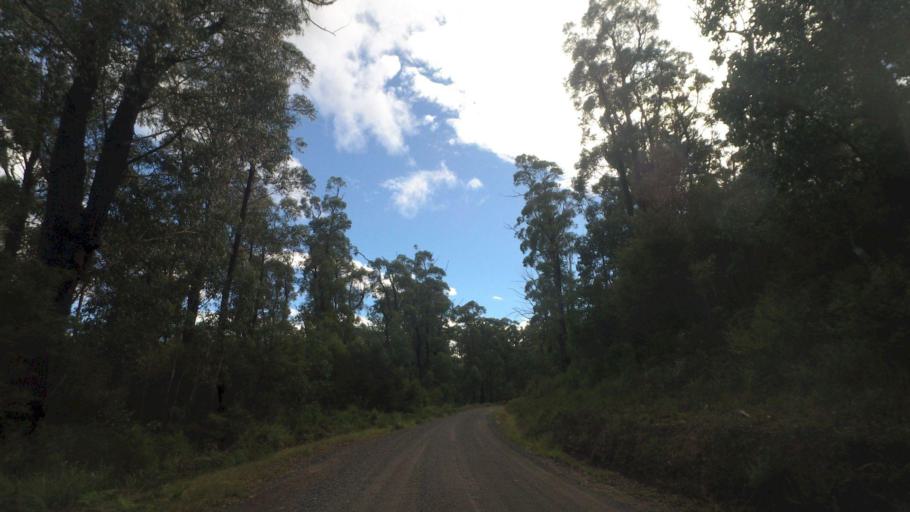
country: AU
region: Victoria
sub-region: Cardinia
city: Bunyip
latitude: -37.9925
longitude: 145.8149
